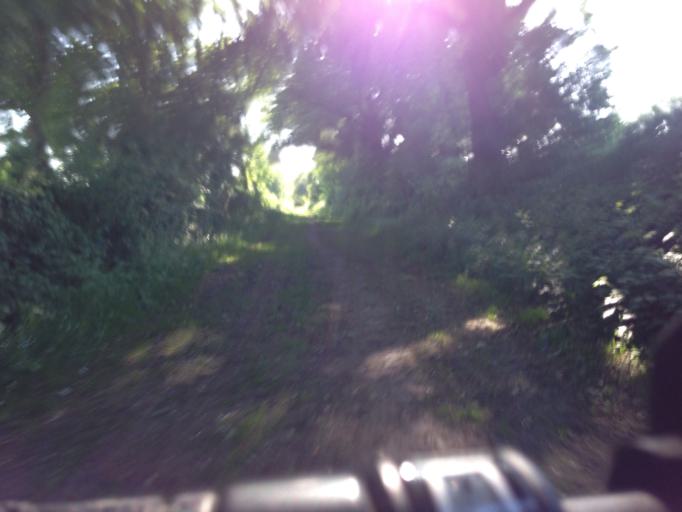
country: DE
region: Schleswig-Holstein
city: Barsbuettel
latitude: 53.5788
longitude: 10.1729
